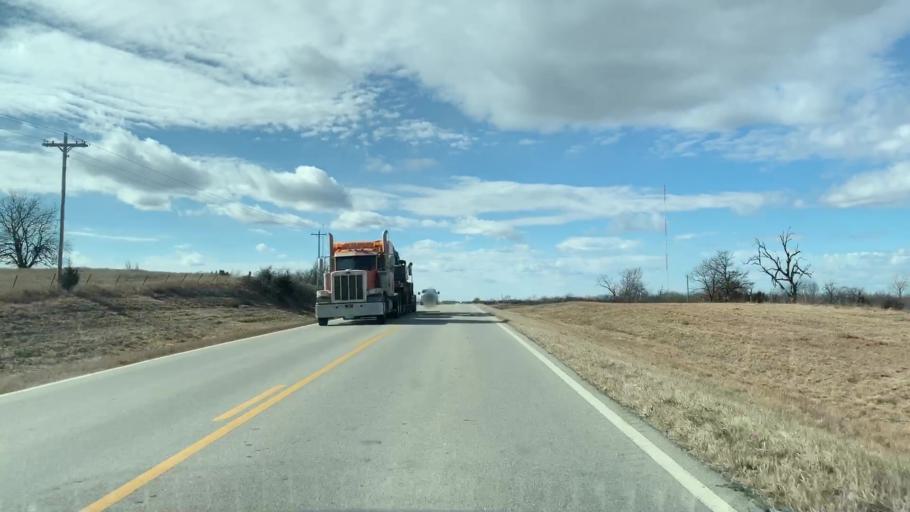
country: US
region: Kansas
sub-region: Neosho County
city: Erie
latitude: 37.5292
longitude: -95.3719
